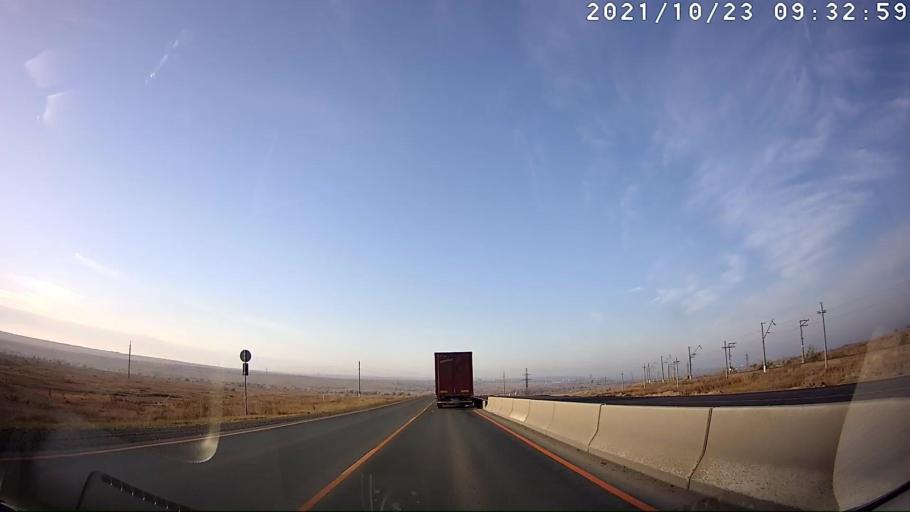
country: RU
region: Saratov
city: Sokolovyy
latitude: 51.6654
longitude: 45.8548
